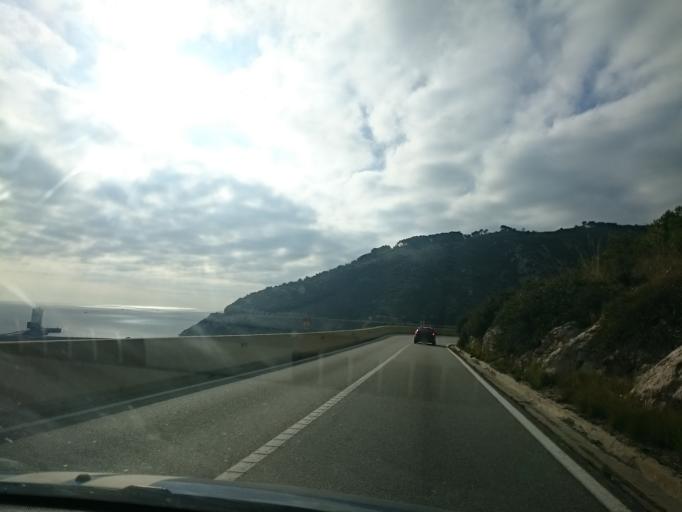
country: ES
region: Catalonia
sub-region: Provincia de Barcelona
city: Sitges
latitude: 41.2442
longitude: 1.8715
